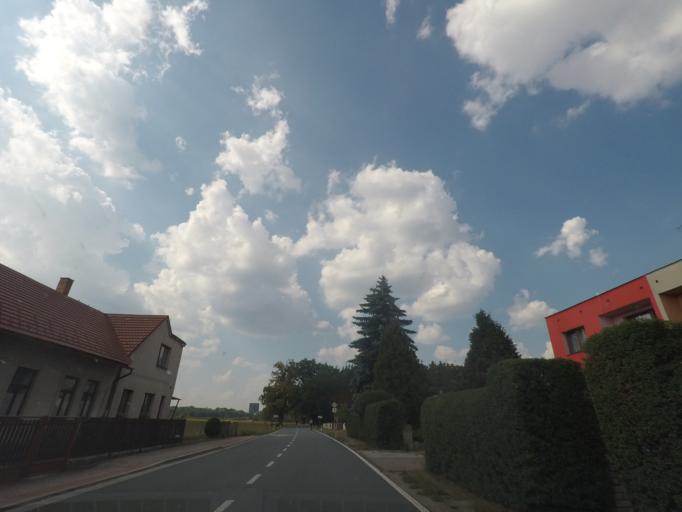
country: CZ
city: Albrechtice nad Orlici
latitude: 50.1215
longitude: 16.0690
